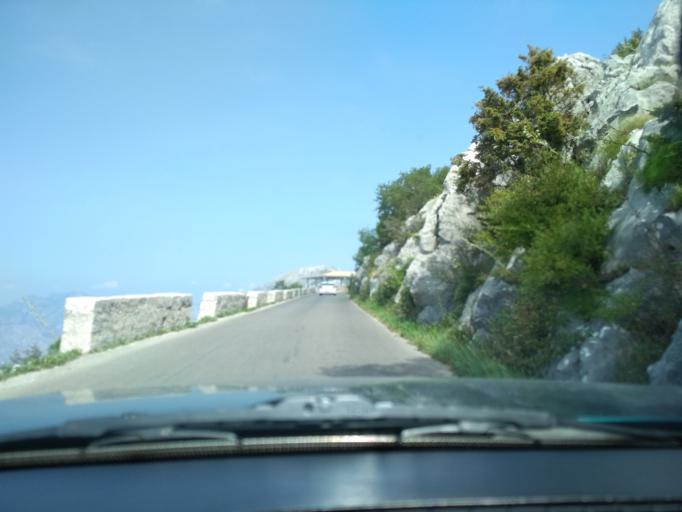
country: ME
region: Kotor
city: Kotor
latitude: 42.4084
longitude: 18.7863
